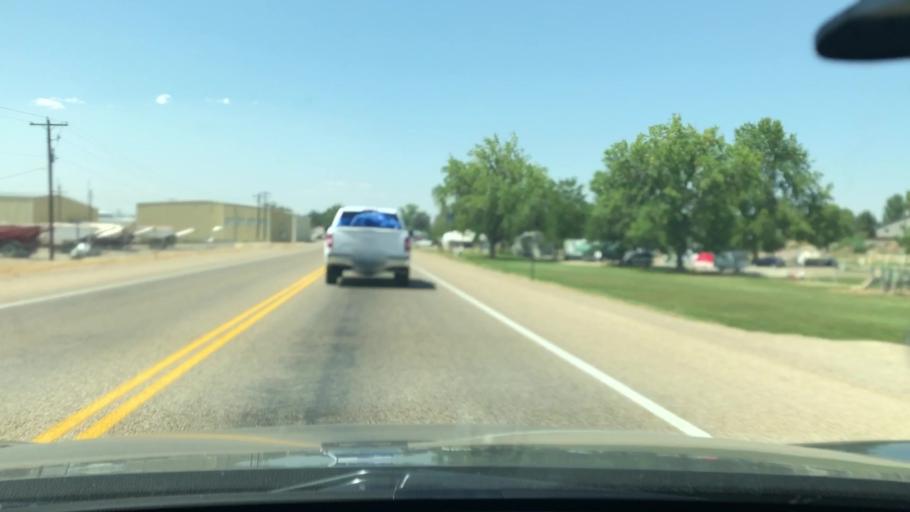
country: US
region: Idaho
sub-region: Canyon County
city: Parma
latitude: 43.7798
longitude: -116.9335
